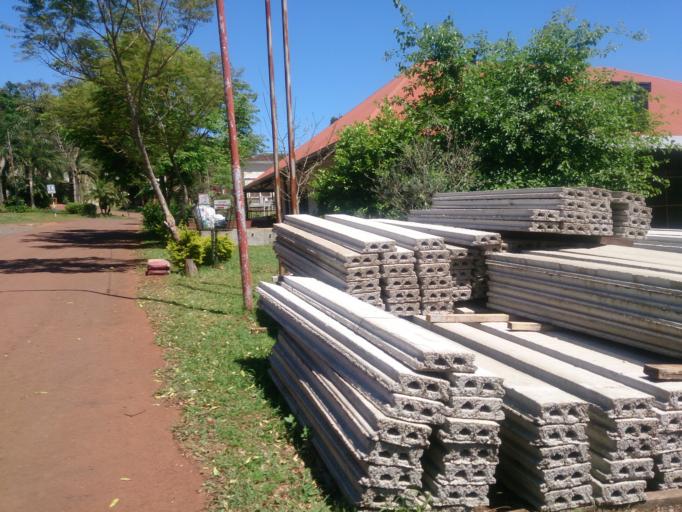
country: AR
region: Misiones
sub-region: Departamento de Obera
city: Obera
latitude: -27.4984
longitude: -55.1131
